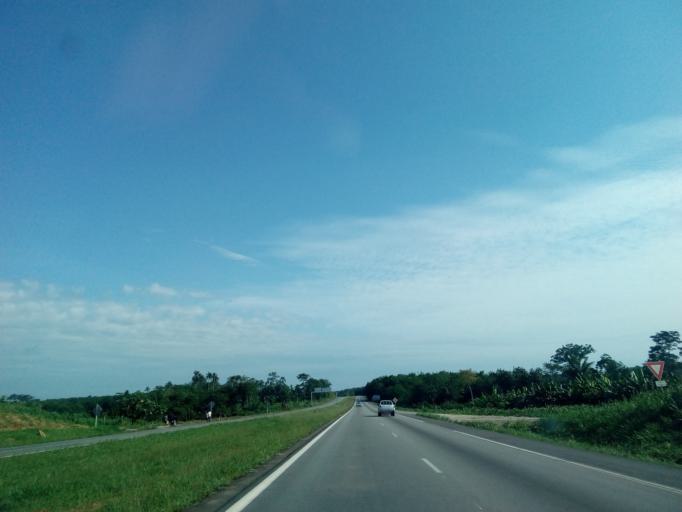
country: CI
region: Lagunes
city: Songon
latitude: 5.5240
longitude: -4.2905
